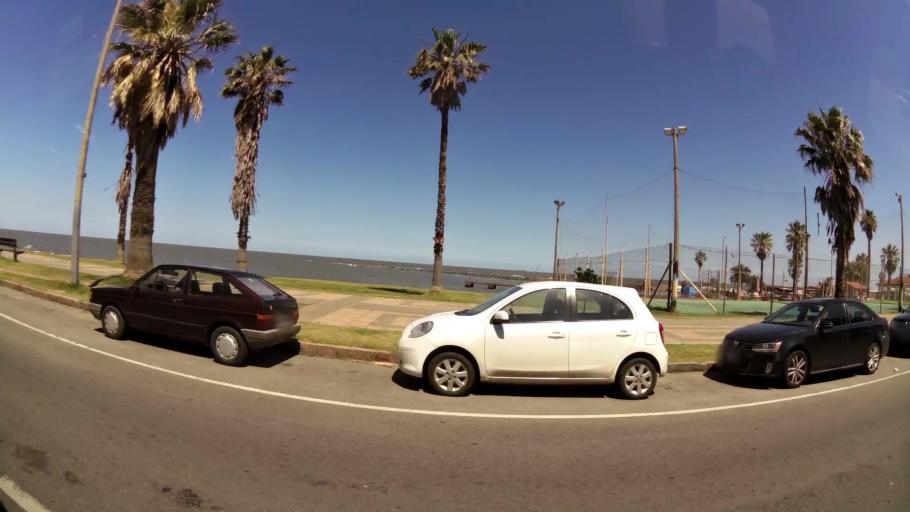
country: UY
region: Montevideo
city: Montevideo
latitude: -34.9227
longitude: -56.1519
